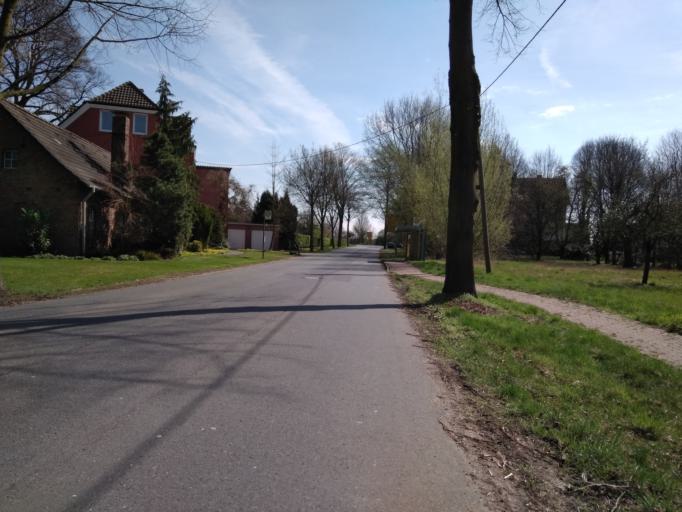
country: DE
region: North Rhine-Westphalia
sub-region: Regierungsbezirk Dusseldorf
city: Schermbeck
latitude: 51.6631
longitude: 6.8831
